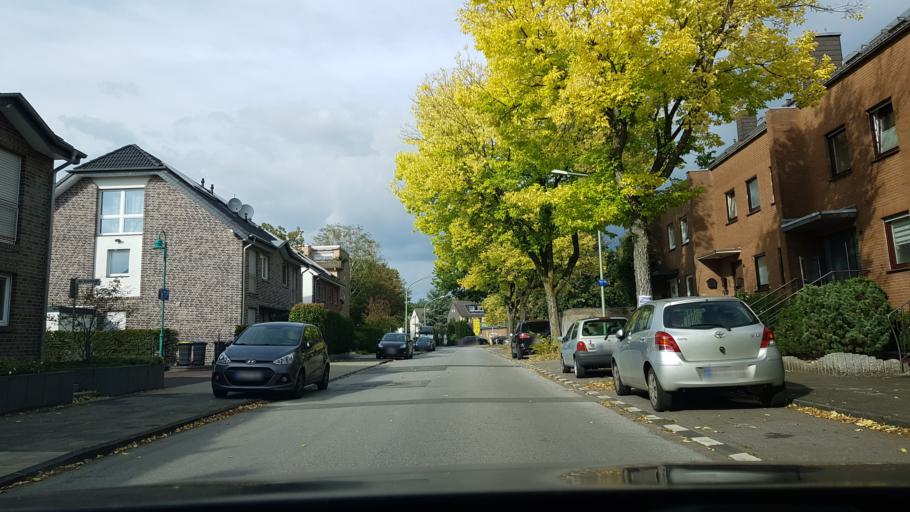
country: DE
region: North Rhine-Westphalia
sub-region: Regierungsbezirk Dusseldorf
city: Hochfeld
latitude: 51.3715
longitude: 6.7846
